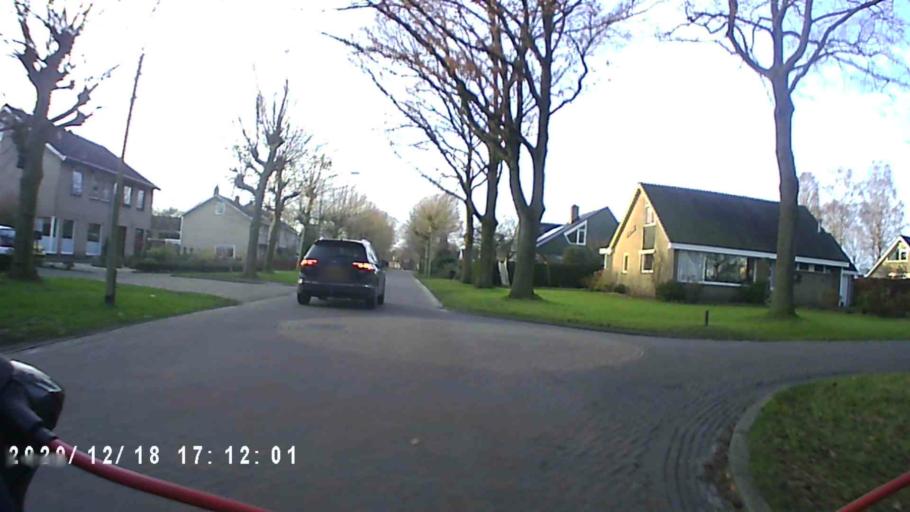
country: NL
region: Drenthe
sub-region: Gemeente Tynaarlo
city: Tynaarlo
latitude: 53.0762
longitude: 6.6240
